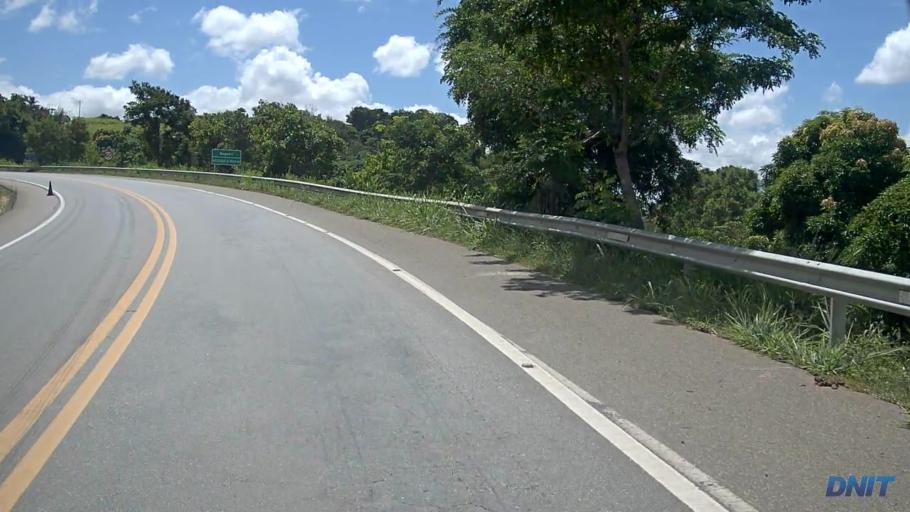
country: BR
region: Minas Gerais
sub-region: Governador Valadares
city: Governador Valadares
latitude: -18.9641
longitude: -42.0787
